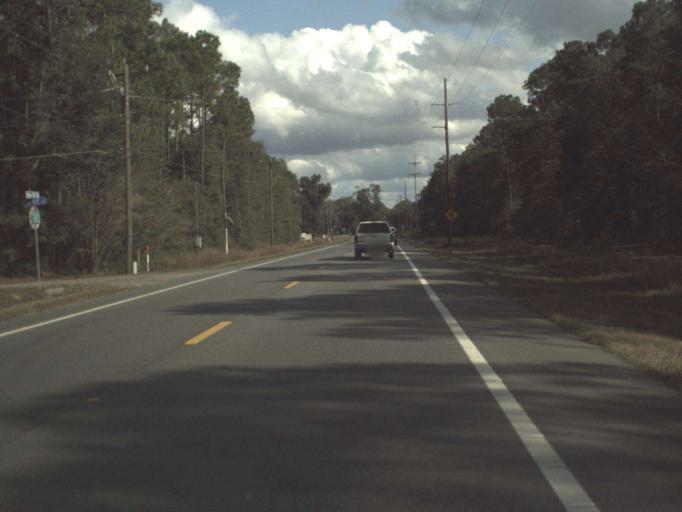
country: US
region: Florida
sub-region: Gadsden County
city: Midway
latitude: 30.4398
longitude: -84.4770
